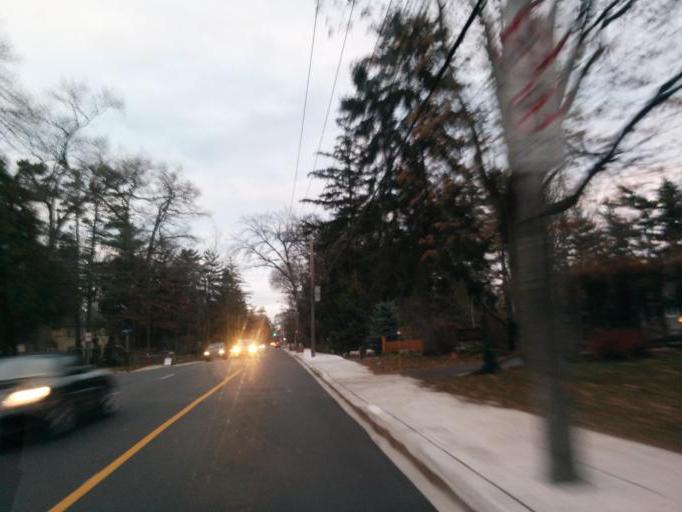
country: CA
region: Ontario
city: Mississauga
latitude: 43.5515
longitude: -79.6054
